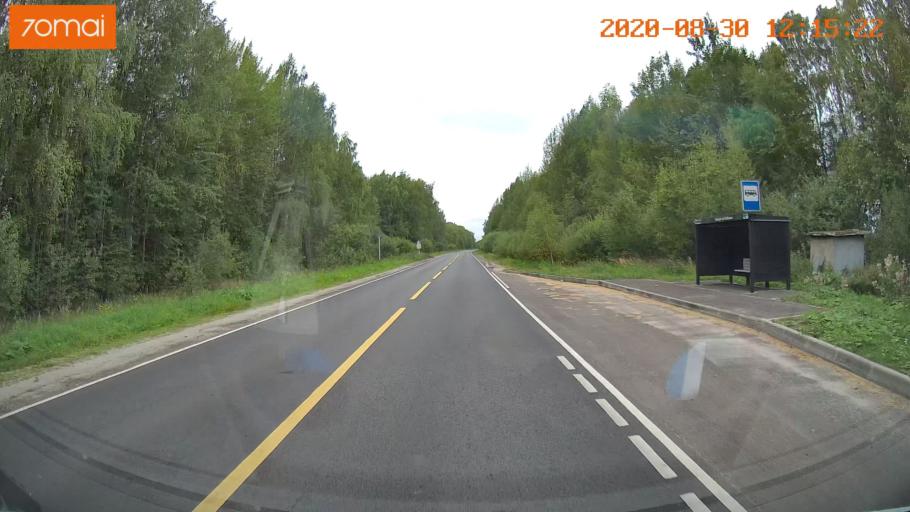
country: RU
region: Ivanovo
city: Yur'yevets
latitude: 57.3170
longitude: 43.0316
